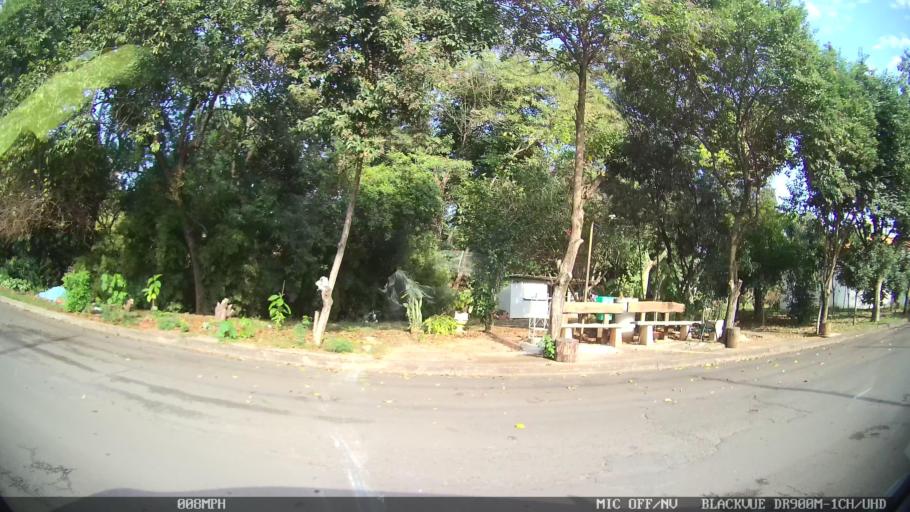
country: BR
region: Sao Paulo
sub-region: Americana
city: Americana
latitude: -22.7349
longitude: -47.3415
